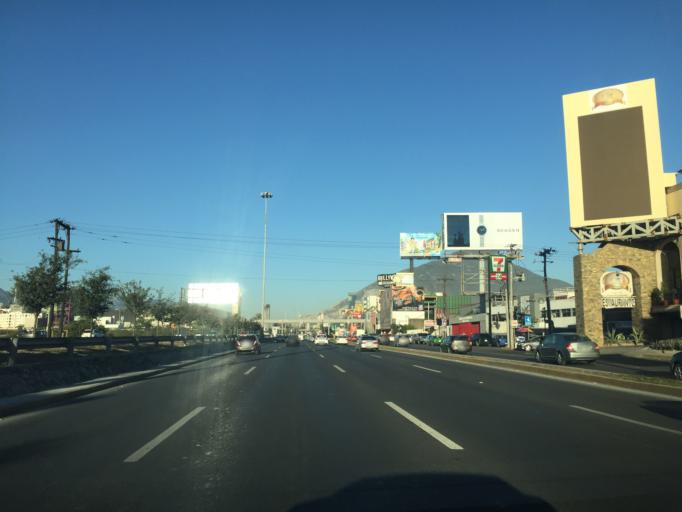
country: MX
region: Nuevo Leon
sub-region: Monterrey
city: Monterrey
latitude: 25.6682
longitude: -100.3359
